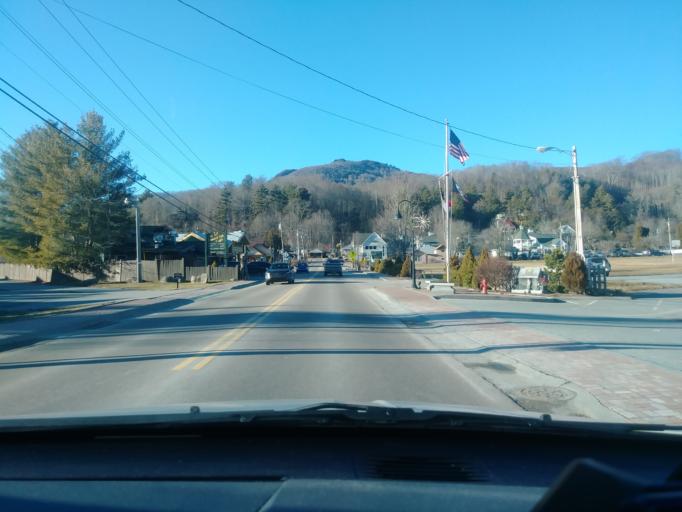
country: US
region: North Carolina
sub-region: Avery County
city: Banner Elk
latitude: 36.1612
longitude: -81.8707
